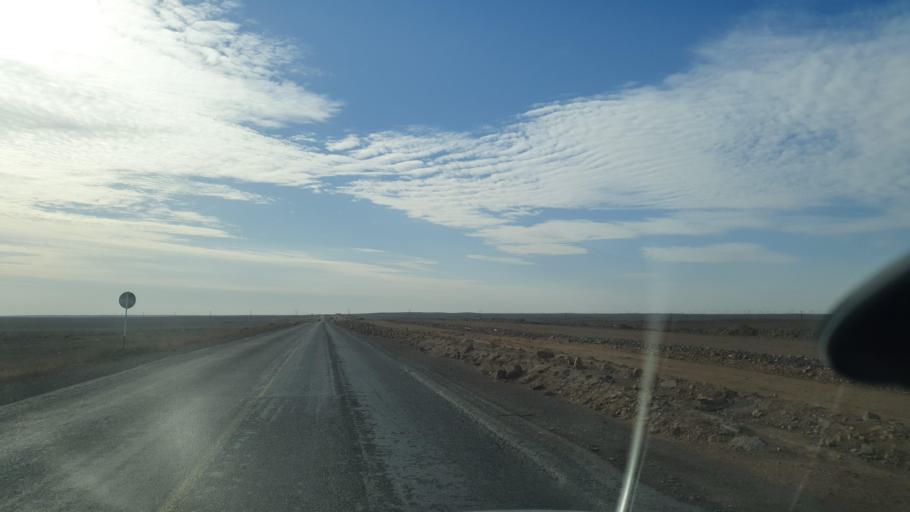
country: KZ
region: Qaraghandy
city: Saryshaghan
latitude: 45.9863
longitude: 73.5649
